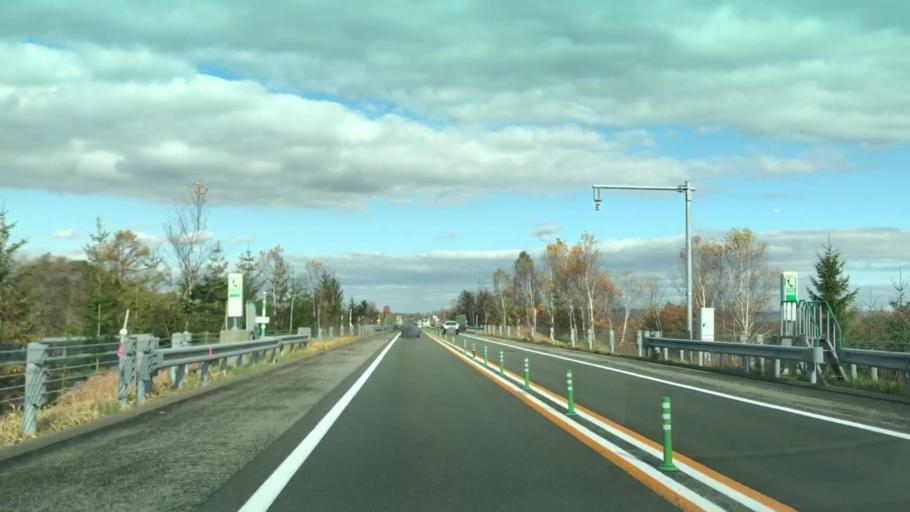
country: JP
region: Hokkaido
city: Chitose
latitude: 42.8733
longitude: 141.6148
